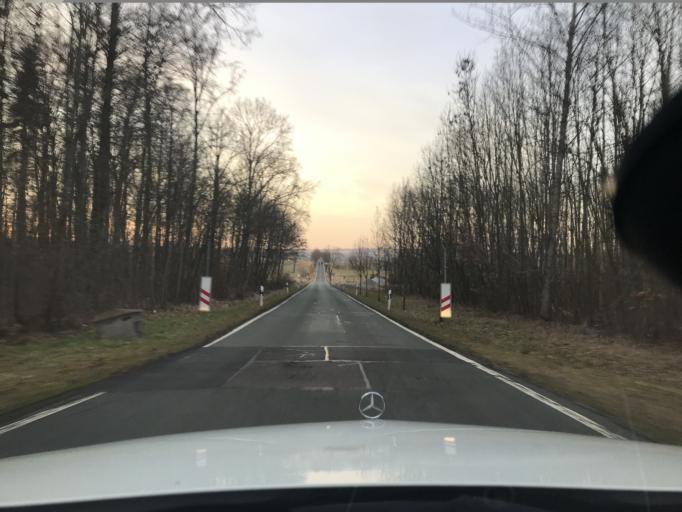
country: DE
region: Thuringia
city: Emleben
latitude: 50.9097
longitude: 10.6533
